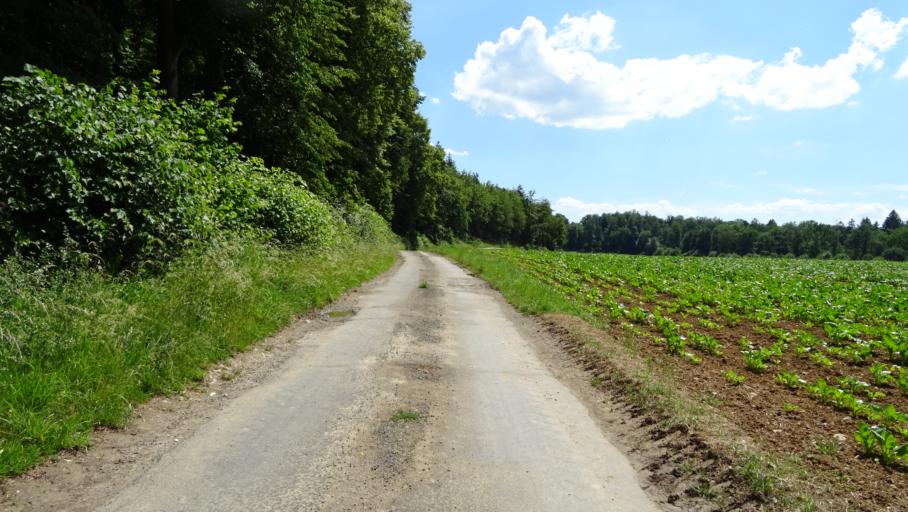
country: DE
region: Baden-Wuerttemberg
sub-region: Karlsruhe Region
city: Adelsheim
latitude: 49.4154
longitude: 9.3674
